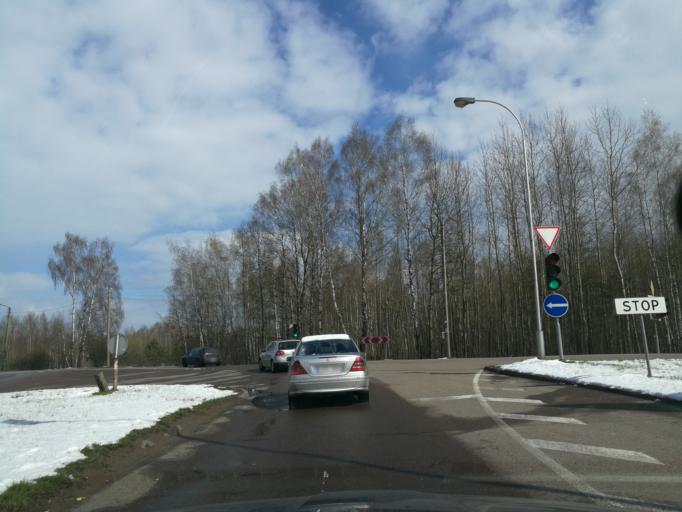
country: LT
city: Ramuciai
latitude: 54.9178
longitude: 24.0356
